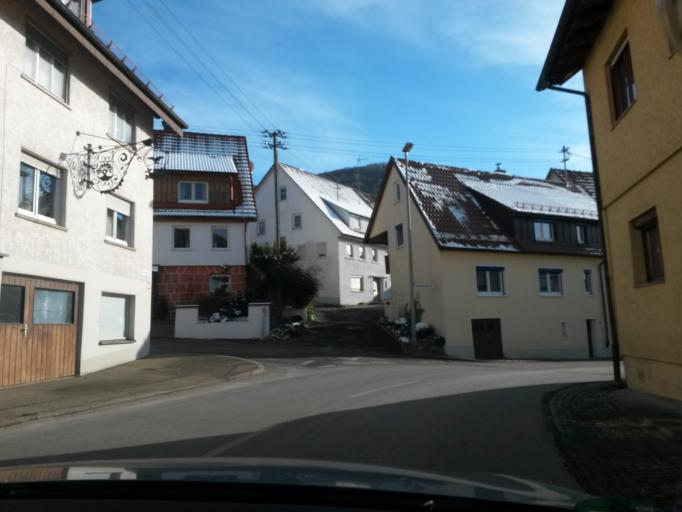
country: DE
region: Baden-Wuerttemberg
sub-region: Regierungsbezirk Stuttgart
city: Gingen an der Fils
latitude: 48.6267
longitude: 9.7615
